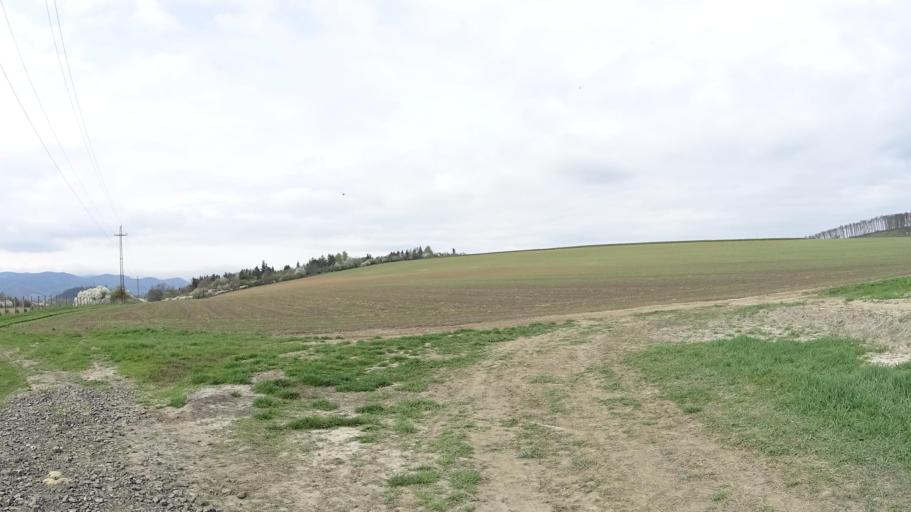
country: HU
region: Nograd
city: Diosjeno
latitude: 47.8937
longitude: 19.0626
